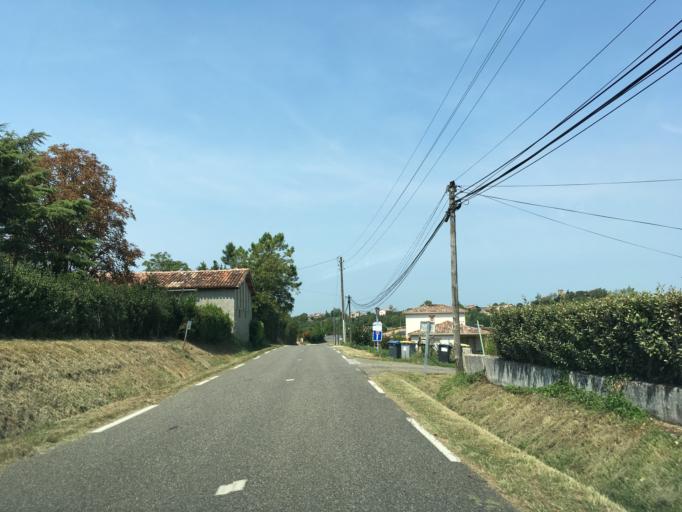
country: FR
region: Midi-Pyrenees
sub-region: Departement du Tarn-et-Garonne
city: Corbarieu
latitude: 43.9565
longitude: 1.3918
